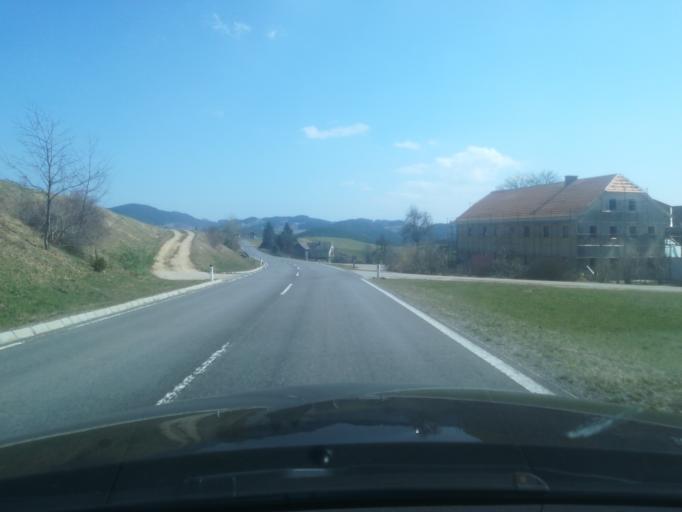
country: AT
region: Upper Austria
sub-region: Politischer Bezirk Perg
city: Bad Kreuzen
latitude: 48.4158
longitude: 14.7447
